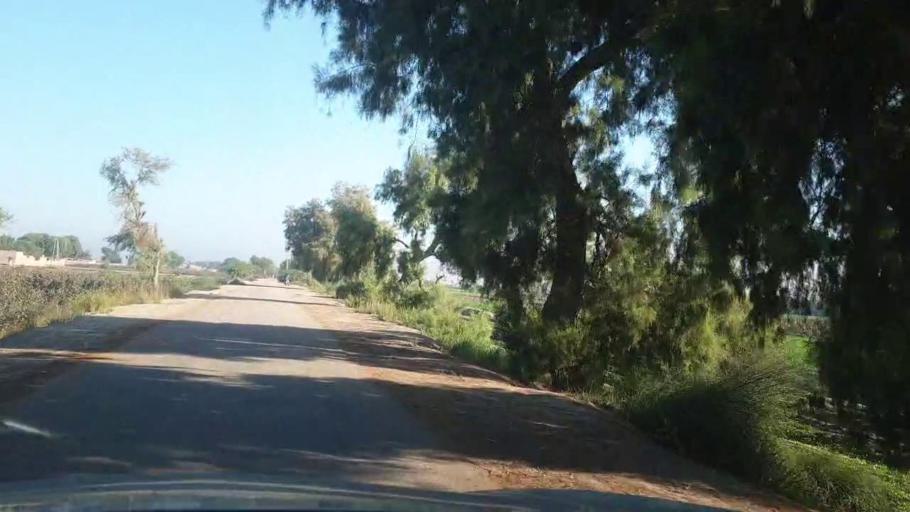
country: PK
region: Sindh
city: Bhan
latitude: 26.5435
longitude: 67.6893
